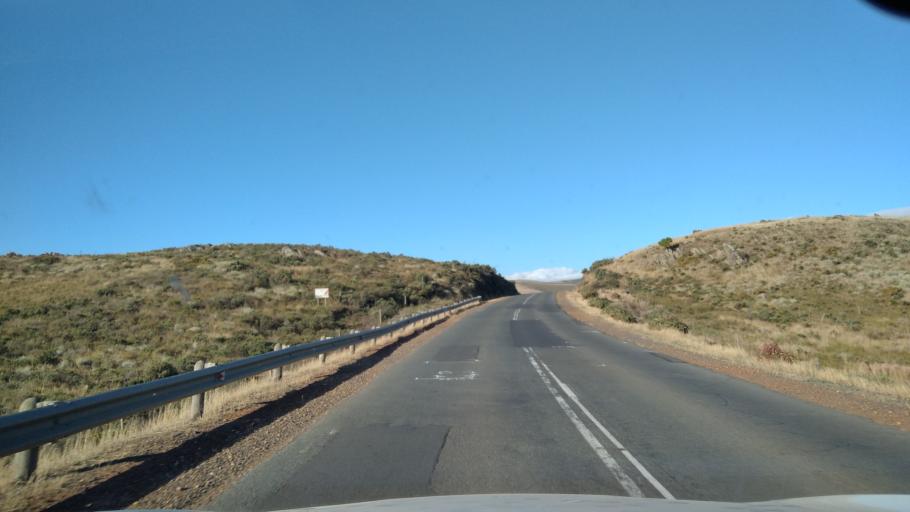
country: ZA
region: Western Cape
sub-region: Overberg District Municipality
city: Caledon
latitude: -34.1776
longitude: 19.2789
